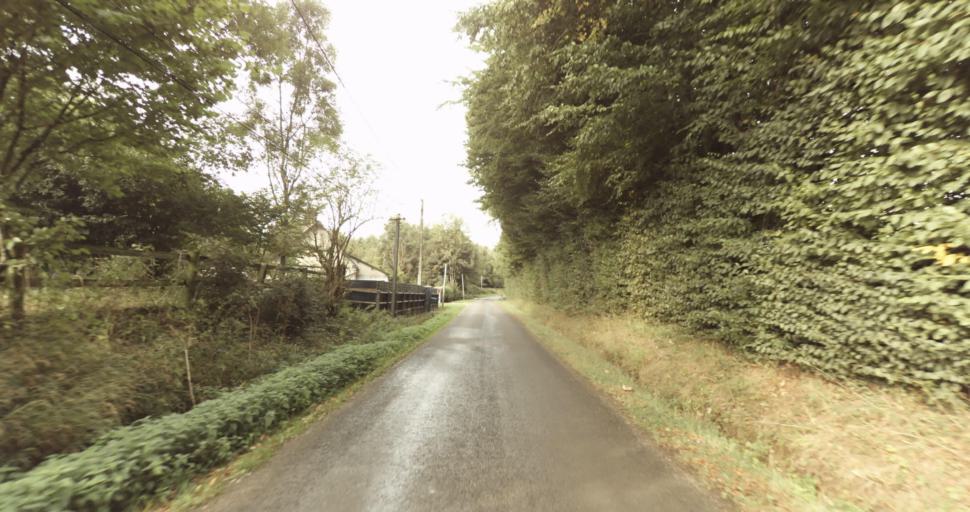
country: FR
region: Lower Normandy
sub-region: Departement de l'Orne
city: Sainte-Gauburge-Sainte-Colombe
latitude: 48.7066
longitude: 0.3708
